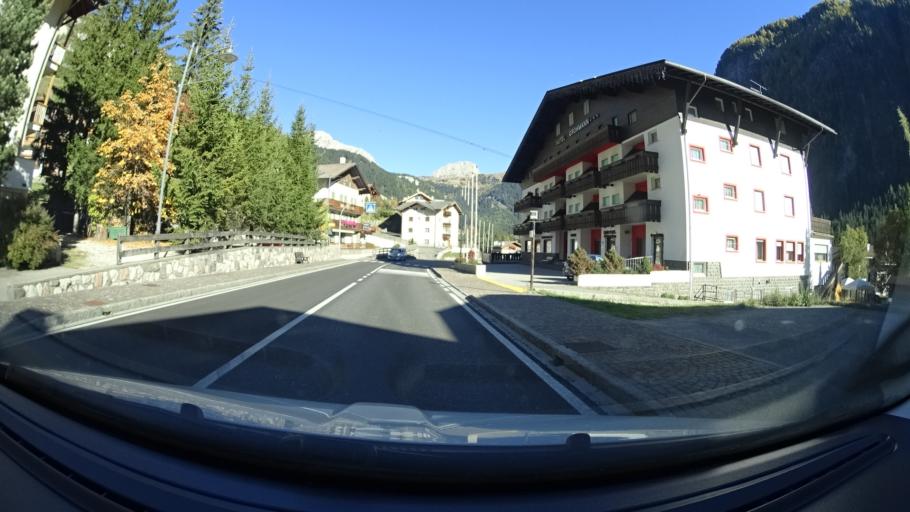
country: IT
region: Trentino-Alto Adige
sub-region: Provincia di Trento
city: Campitello di Fassa
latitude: 46.4767
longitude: 11.7429
